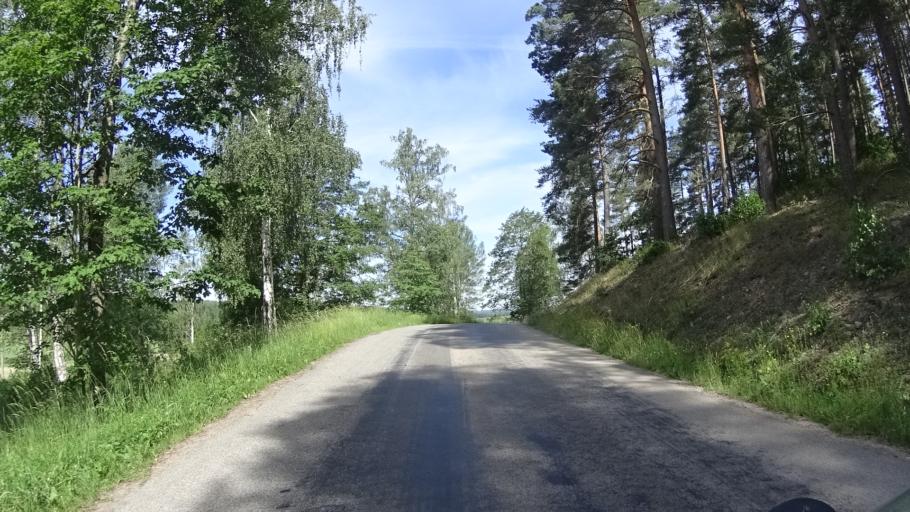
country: SE
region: Kalmar
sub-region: Vasterviks Kommun
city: Overum
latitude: 57.8739
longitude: 16.1748
